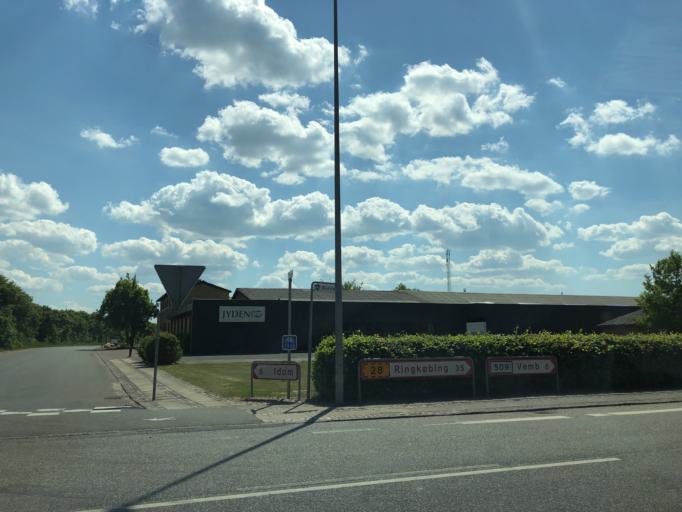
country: DK
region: Central Jutland
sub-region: Holstebro Kommune
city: Ulfborg
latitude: 56.3661
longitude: 8.4291
